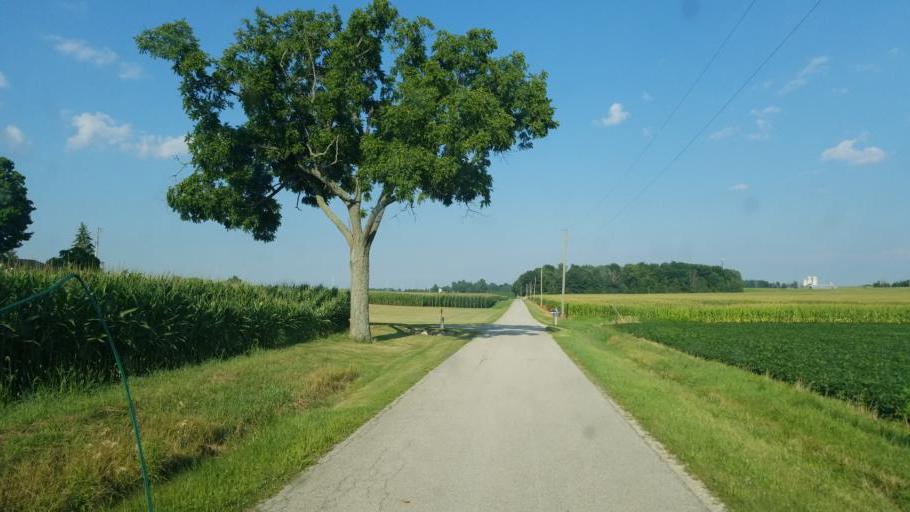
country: US
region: Ohio
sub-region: Crawford County
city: Bucyrus
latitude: 40.8488
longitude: -82.9460
